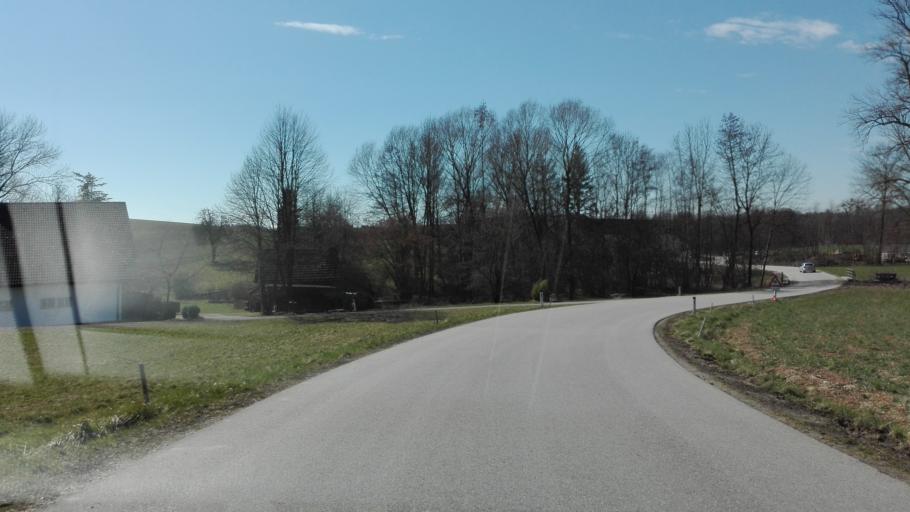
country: AT
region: Upper Austria
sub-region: Wels-Land
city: Buchkirchen
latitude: 48.2277
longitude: 13.9750
